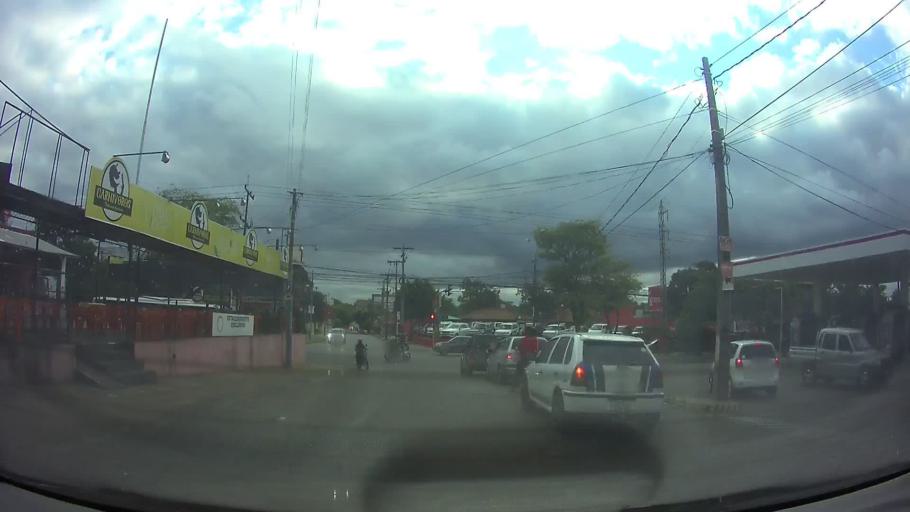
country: PY
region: Central
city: Fernando de la Mora
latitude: -25.3107
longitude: -57.5301
